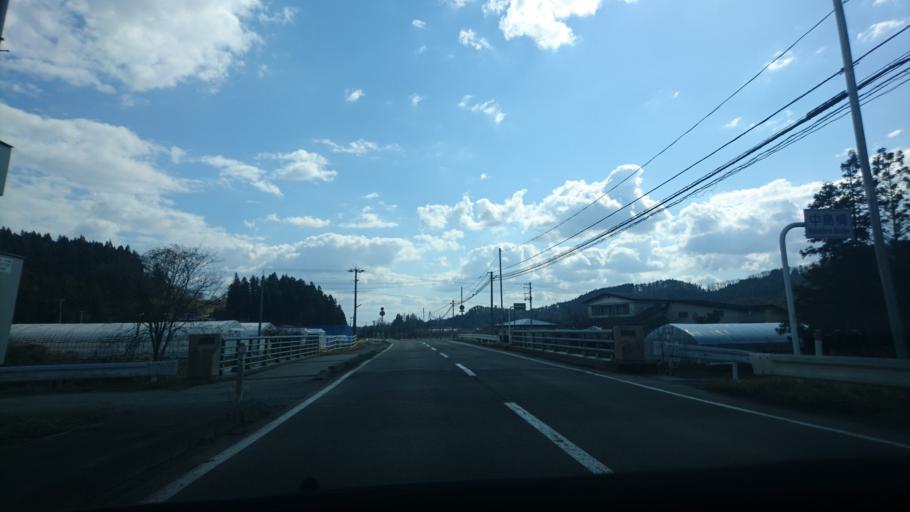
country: JP
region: Iwate
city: Kitakami
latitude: 39.2488
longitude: 141.2042
